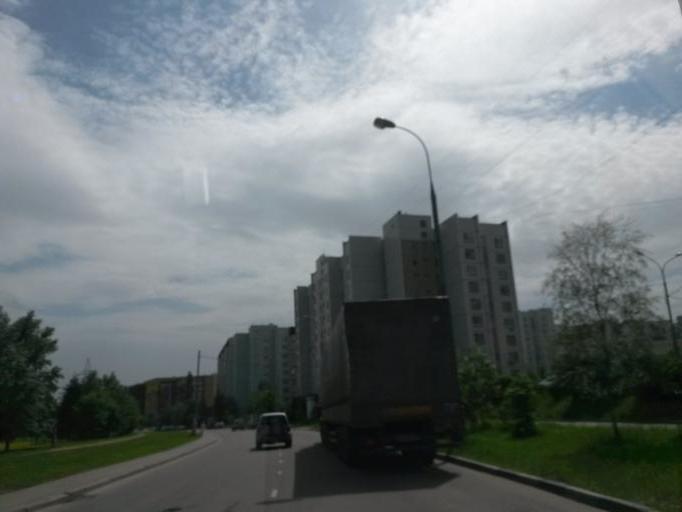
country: RU
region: Moskovskaya
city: Kommunarka
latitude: 55.5471
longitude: 37.5233
